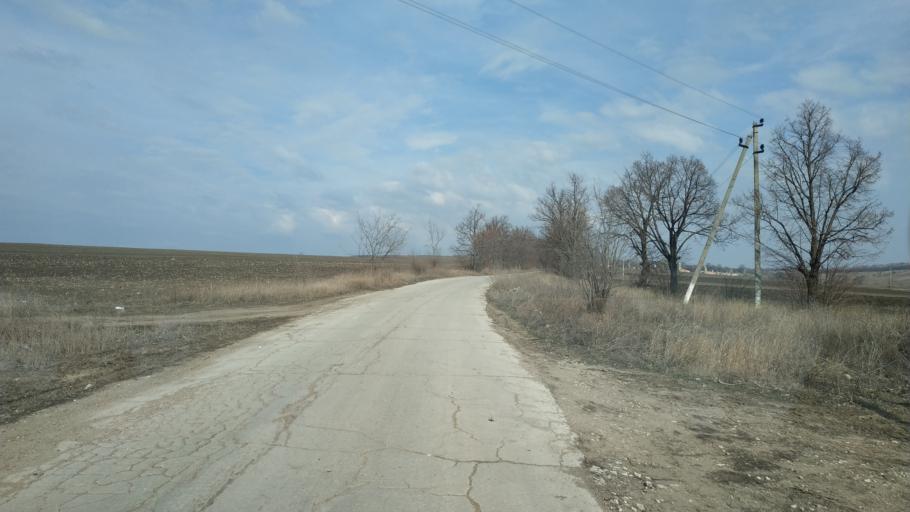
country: MD
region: Anenii Noi
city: Anenii Noi
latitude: 46.9343
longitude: 29.1073
